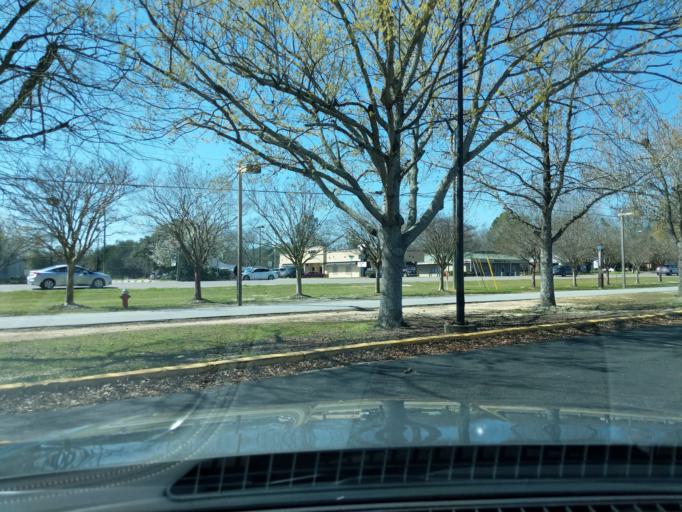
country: US
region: South Carolina
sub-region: Aiken County
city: Aiken
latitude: 33.5269
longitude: -81.7211
